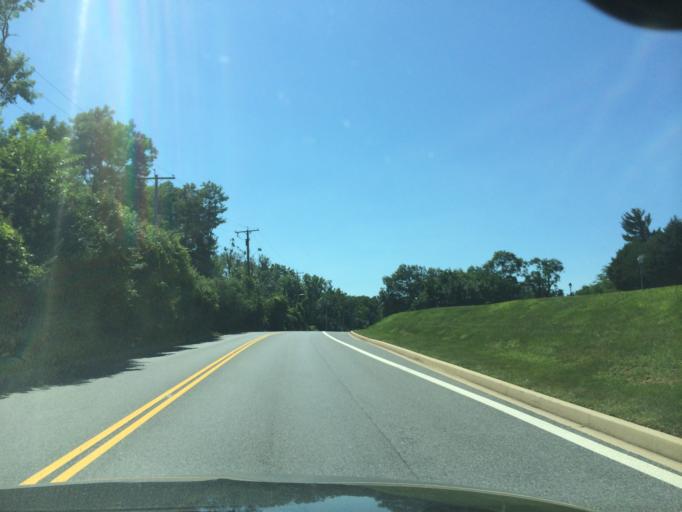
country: US
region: Maryland
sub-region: Baltimore County
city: Mays Chapel
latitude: 39.4207
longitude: -76.6719
